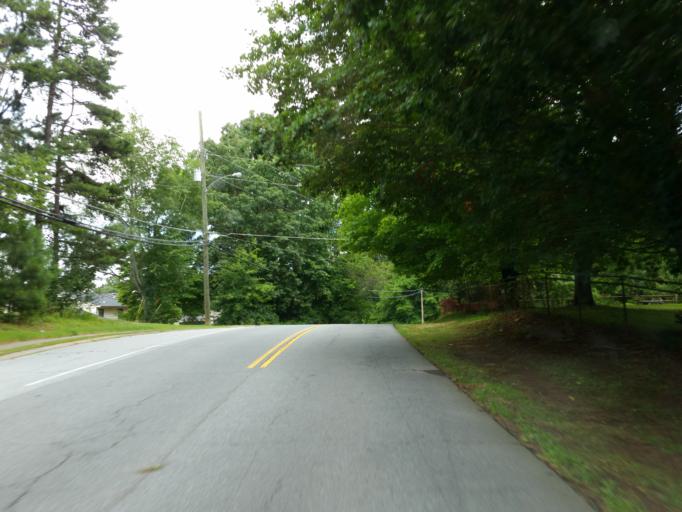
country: US
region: Georgia
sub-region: Cobb County
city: Kennesaw
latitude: 34.0407
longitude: -84.5998
